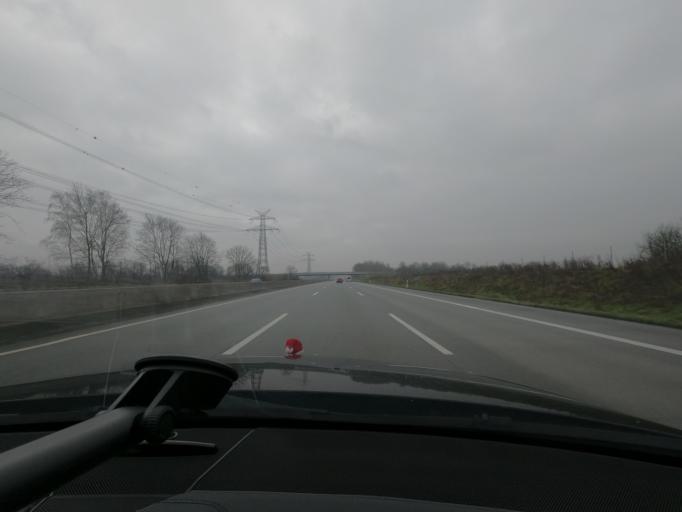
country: DE
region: Schleswig-Holstein
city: Alveslohe
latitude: 53.7763
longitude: 9.9432
